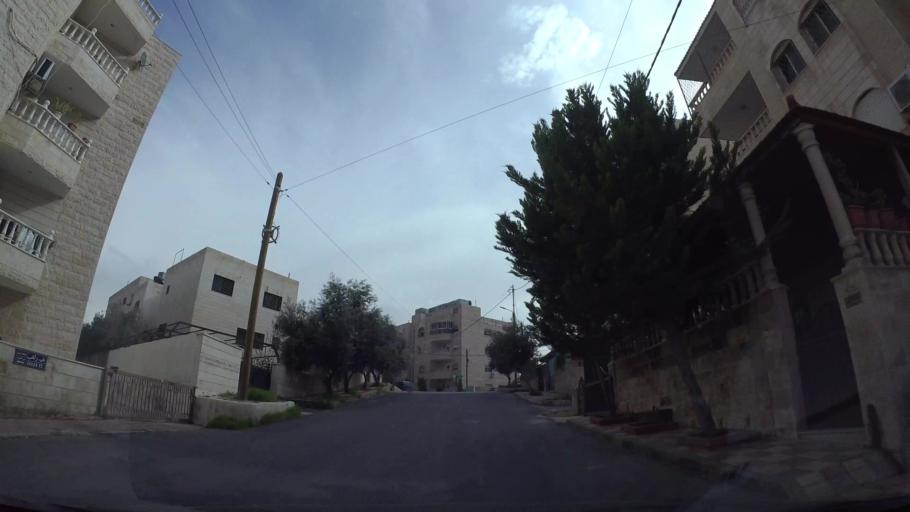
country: JO
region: Amman
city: Amman
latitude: 32.0082
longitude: 35.9398
